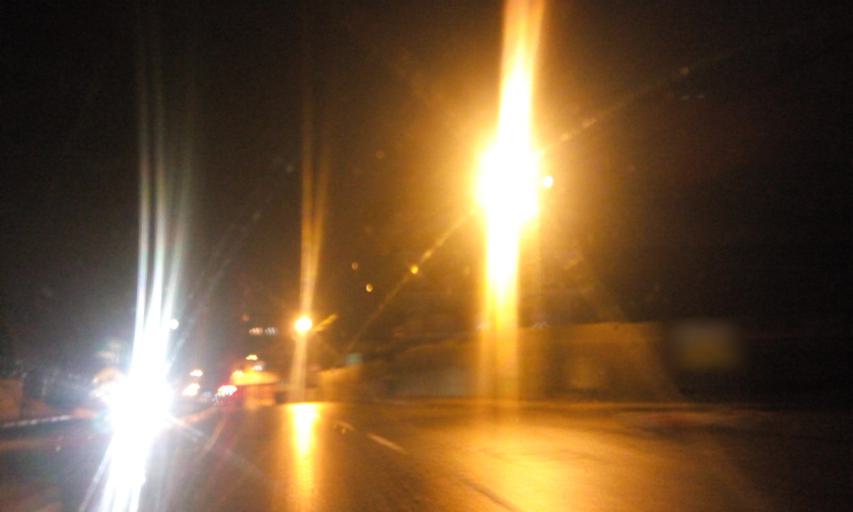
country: TR
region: Istanbul
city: Sultanbeyli
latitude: 40.9360
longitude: 29.2729
